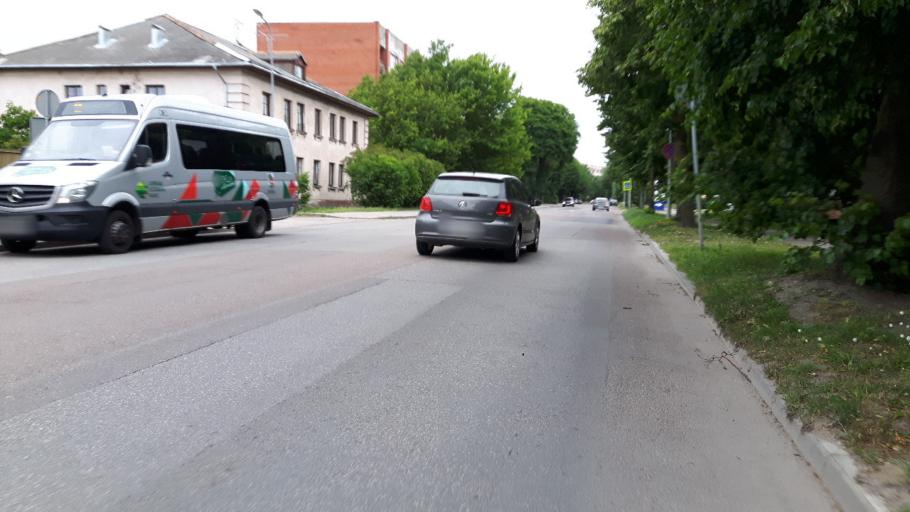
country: LV
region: Liepaja
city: Vec-Liepaja
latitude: 56.5327
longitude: 21.0026
